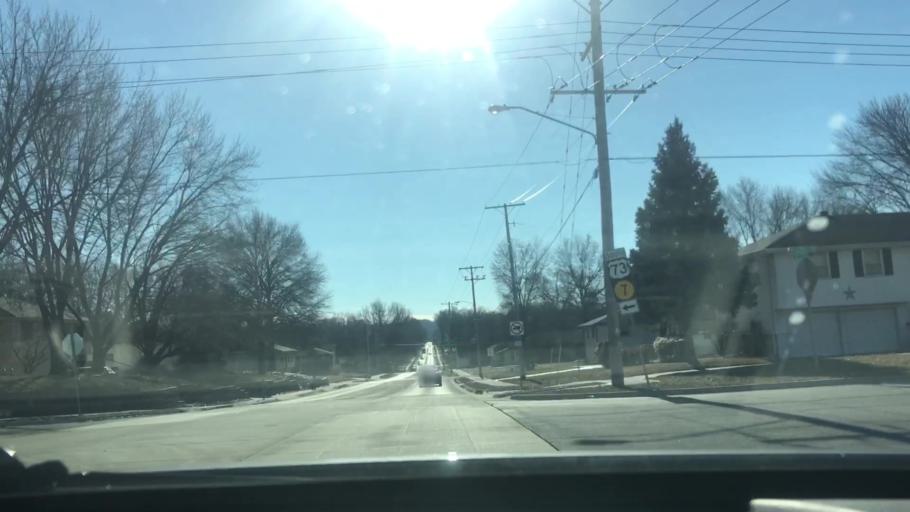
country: US
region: Kansas
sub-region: Leavenworth County
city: Leavenworth
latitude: 39.3271
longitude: -94.9506
